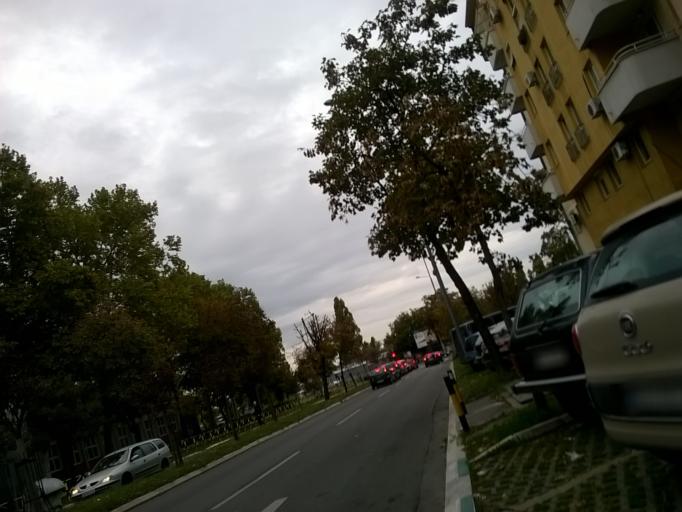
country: RS
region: Central Serbia
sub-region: Belgrade
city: Stari Grad
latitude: 44.8183
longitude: 20.4768
